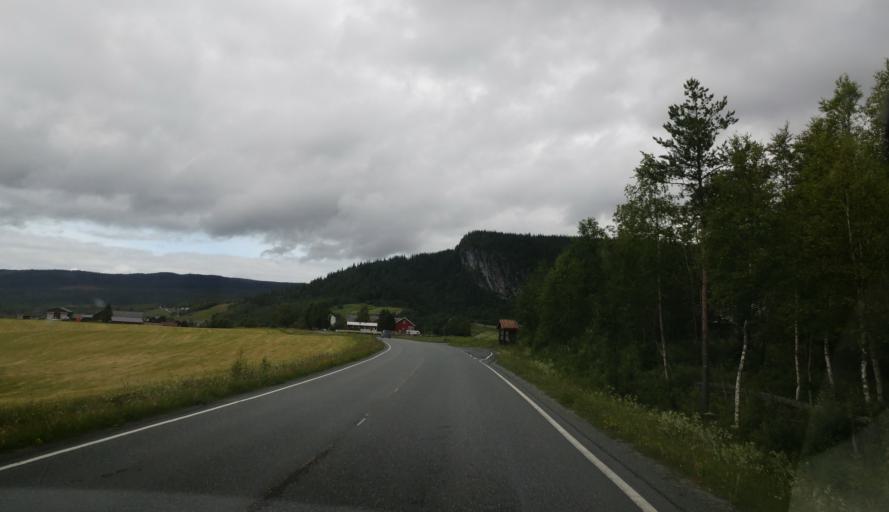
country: NO
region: Sor-Trondelag
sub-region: Selbu
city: Mebonden
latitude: 63.3809
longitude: 11.0824
